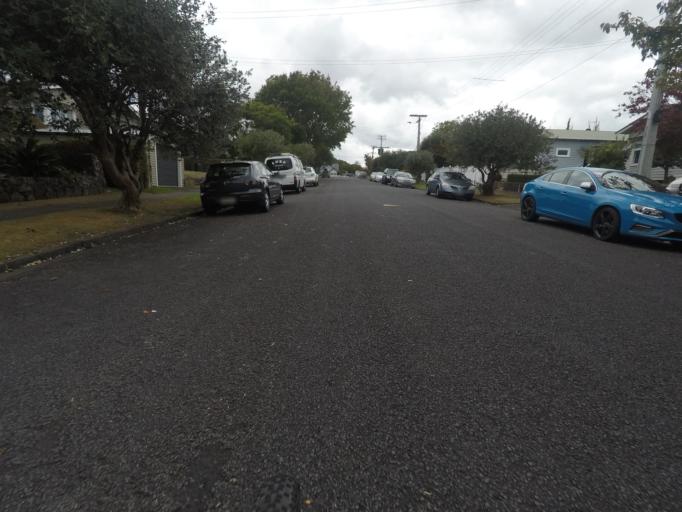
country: NZ
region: Auckland
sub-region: Auckland
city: Auckland
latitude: -36.8747
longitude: 174.7190
